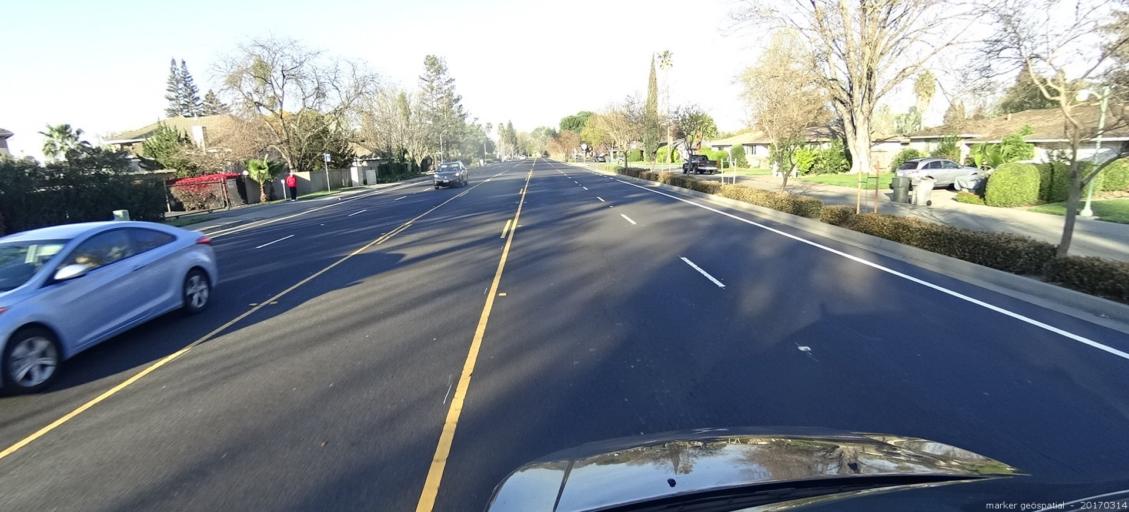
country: US
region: California
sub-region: Yolo County
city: West Sacramento
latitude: 38.5131
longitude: -121.5345
